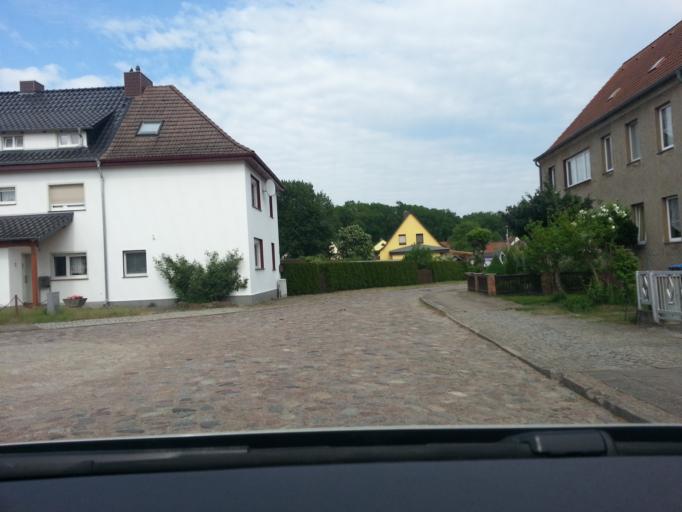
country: DE
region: Mecklenburg-Vorpommern
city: Torgelow
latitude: 53.6377
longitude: 14.0044
